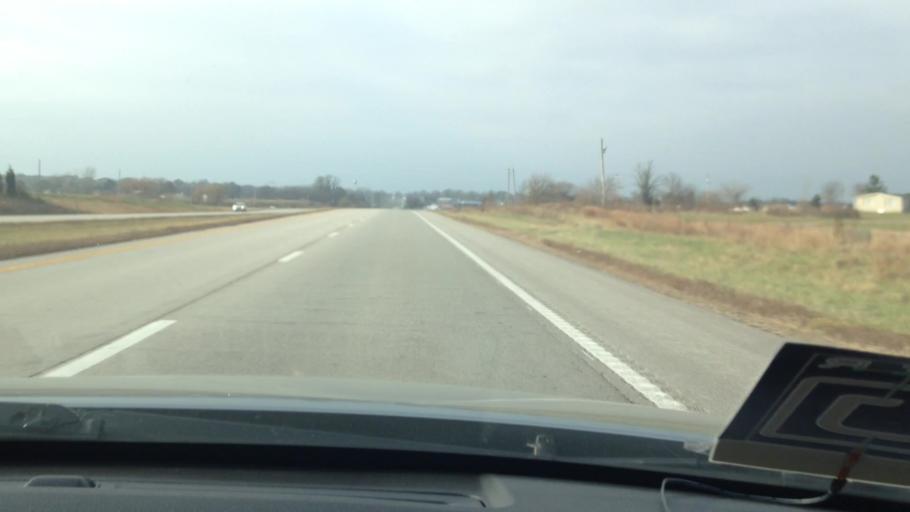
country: US
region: Missouri
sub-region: Cass County
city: Garden City
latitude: 38.5504
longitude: -94.1740
